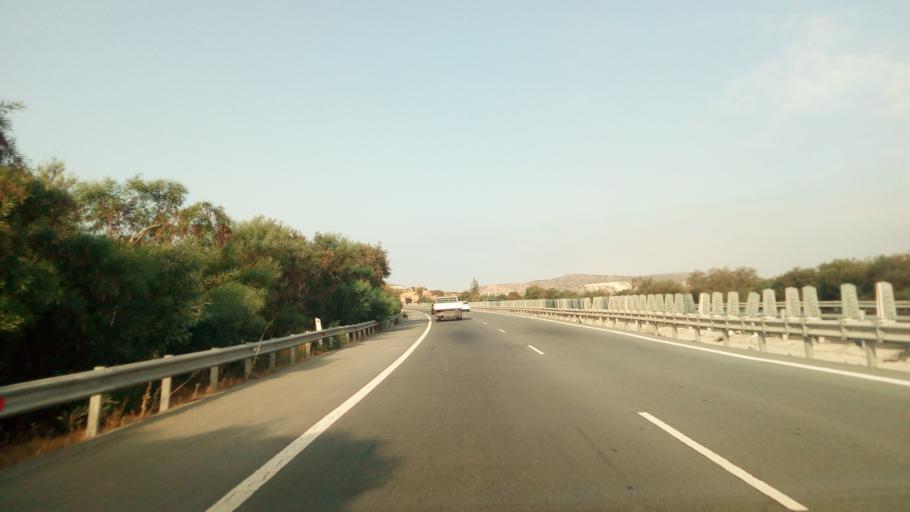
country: CY
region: Limassol
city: Pyrgos
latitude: 34.7327
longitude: 33.2134
